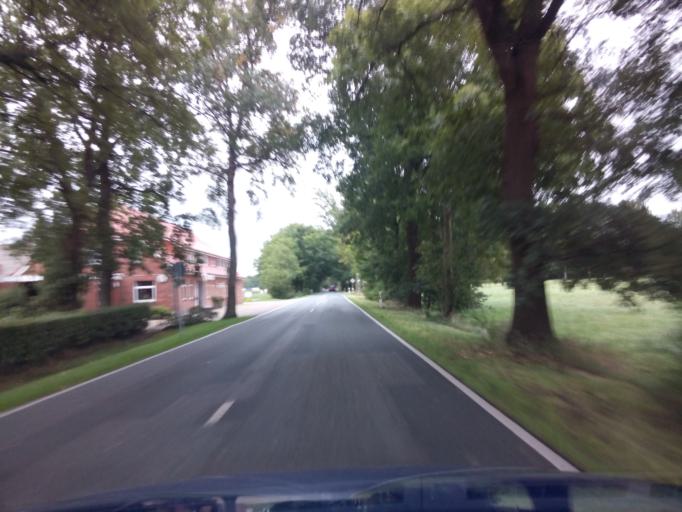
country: DE
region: Lower Saxony
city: Beverstedt
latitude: 53.4730
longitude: 8.8511
